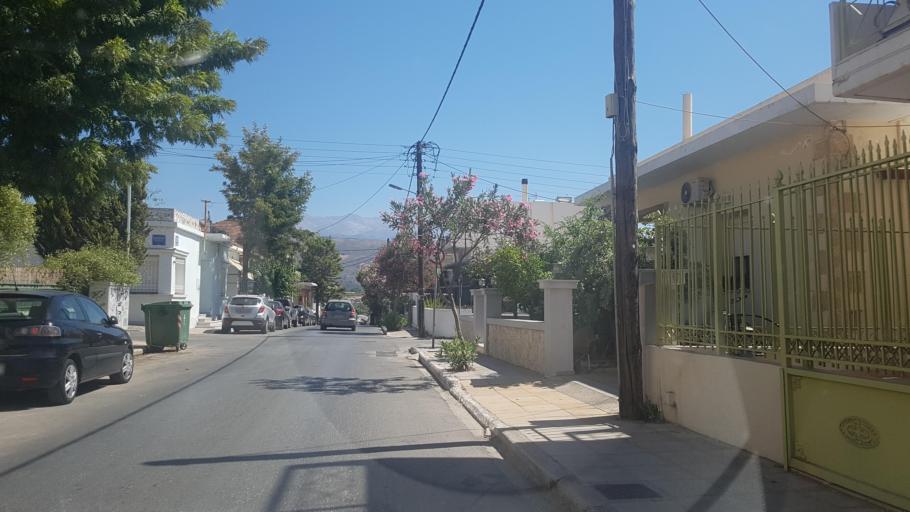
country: GR
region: Crete
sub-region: Nomos Chanias
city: Chania
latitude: 35.5061
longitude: 24.0177
